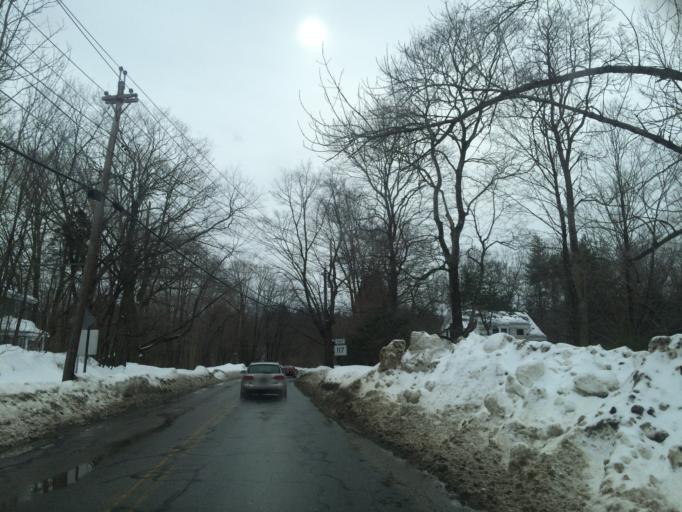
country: US
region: Massachusetts
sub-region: Middlesex County
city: Lincoln
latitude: 42.4043
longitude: -71.3203
